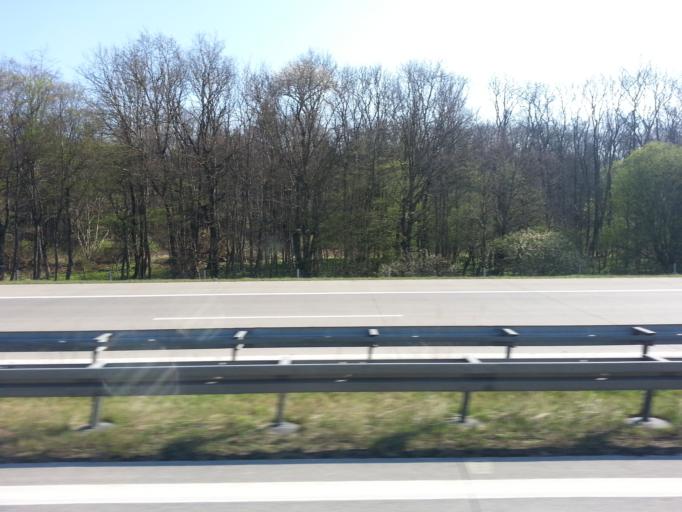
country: DE
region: Mecklenburg-Vorpommern
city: Laage
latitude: 53.8942
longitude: 12.2549
